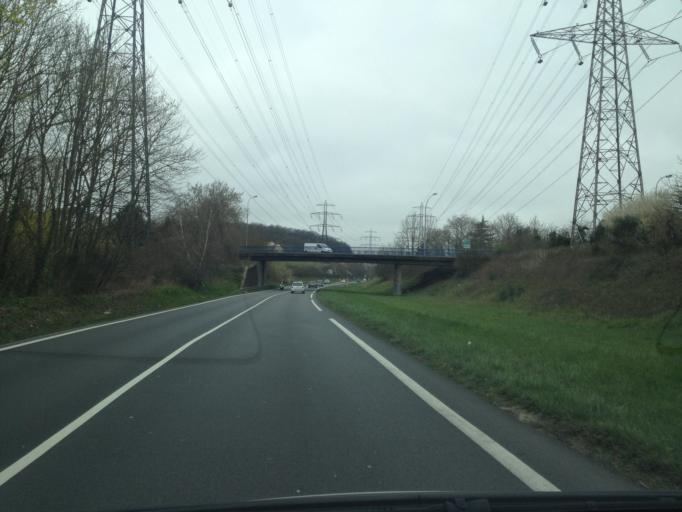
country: FR
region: Ile-de-France
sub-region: Departement de l'Essonne
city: Igny
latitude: 48.7368
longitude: 2.2281
